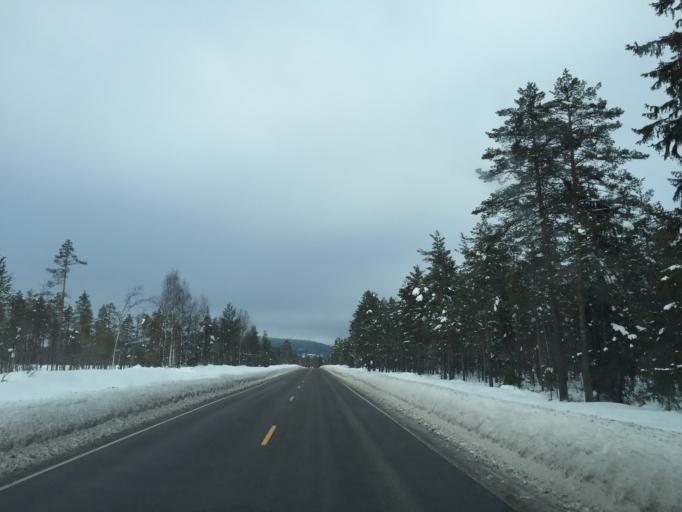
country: NO
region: Hedmark
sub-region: Trysil
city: Innbygda
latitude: 61.1506
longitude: 12.1308
